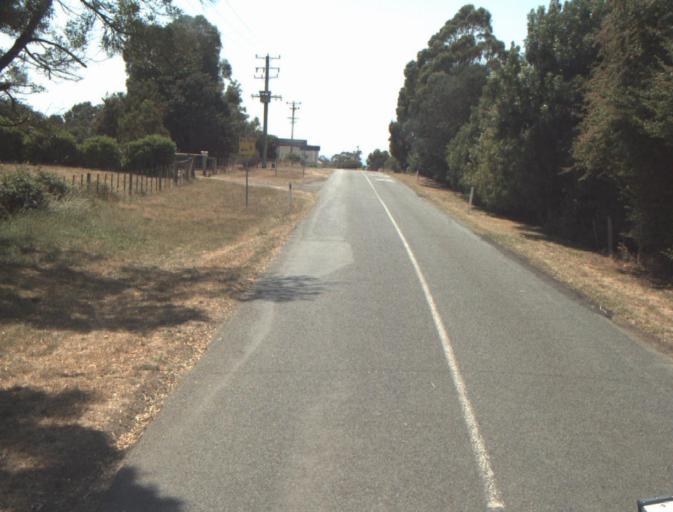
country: AU
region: Tasmania
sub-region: Northern Midlands
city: Perth
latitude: -41.5057
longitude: 147.2022
